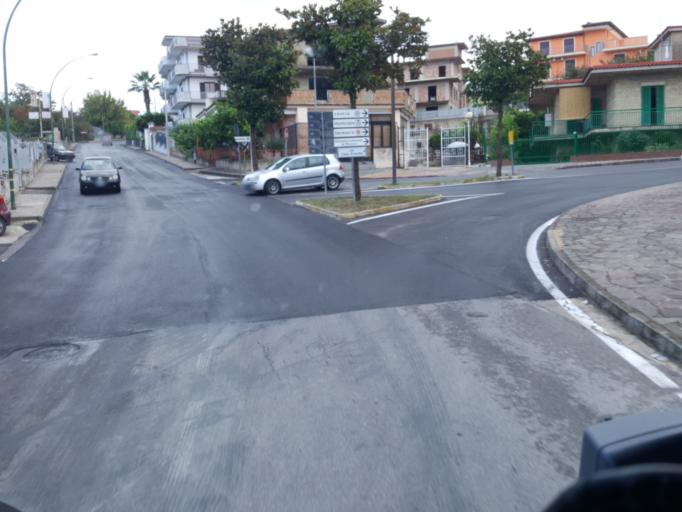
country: IT
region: Campania
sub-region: Provincia di Avellino
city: Domicella
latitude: 40.8804
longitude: 14.5860
